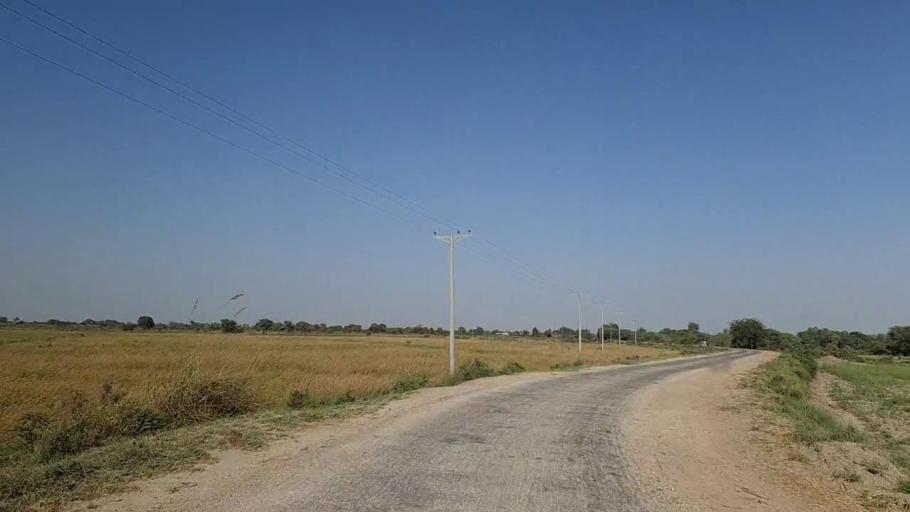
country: PK
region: Sindh
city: Chuhar Jamali
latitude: 24.5215
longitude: 68.0948
